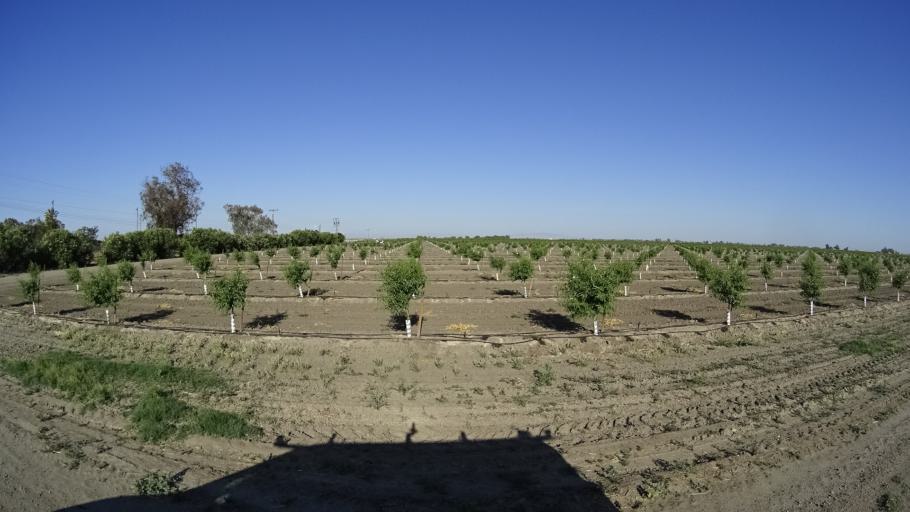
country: US
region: California
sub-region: Kings County
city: Stratford
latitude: 36.1750
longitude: -119.7983
